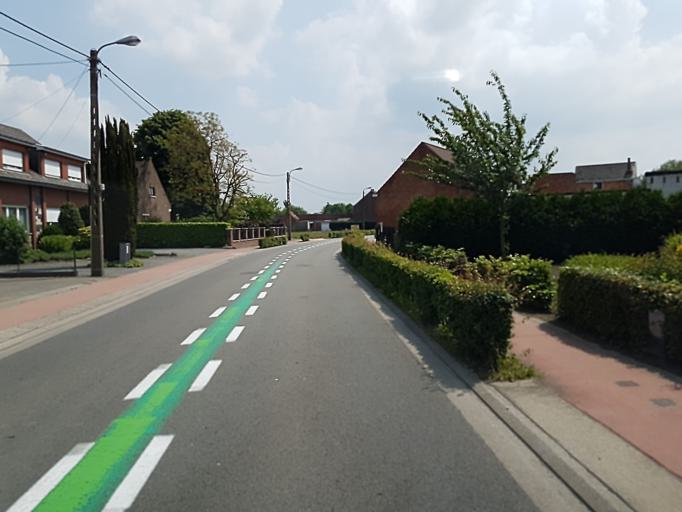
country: BE
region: Flanders
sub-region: Provincie Vlaams-Brabant
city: Londerzeel
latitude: 51.0201
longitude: 4.3147
